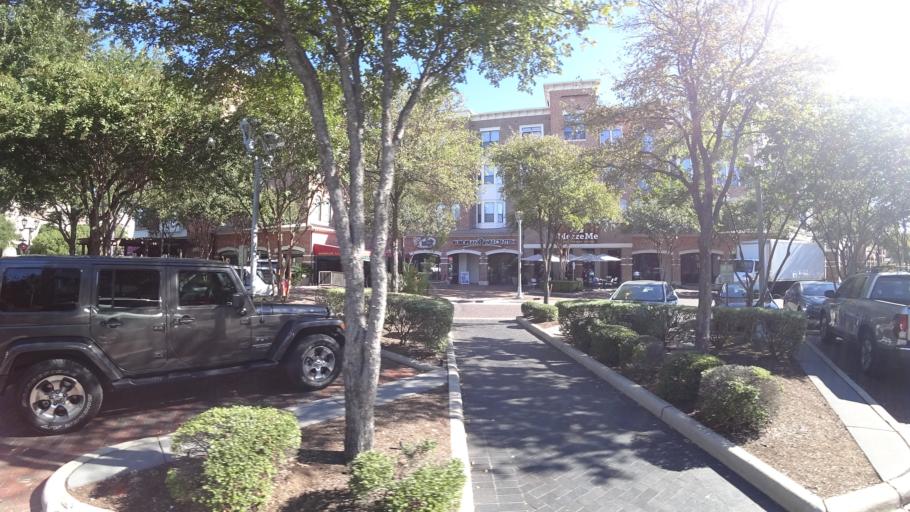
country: US
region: Texas
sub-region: Travis County
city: Austin
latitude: 30.3156
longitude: -97.7338
